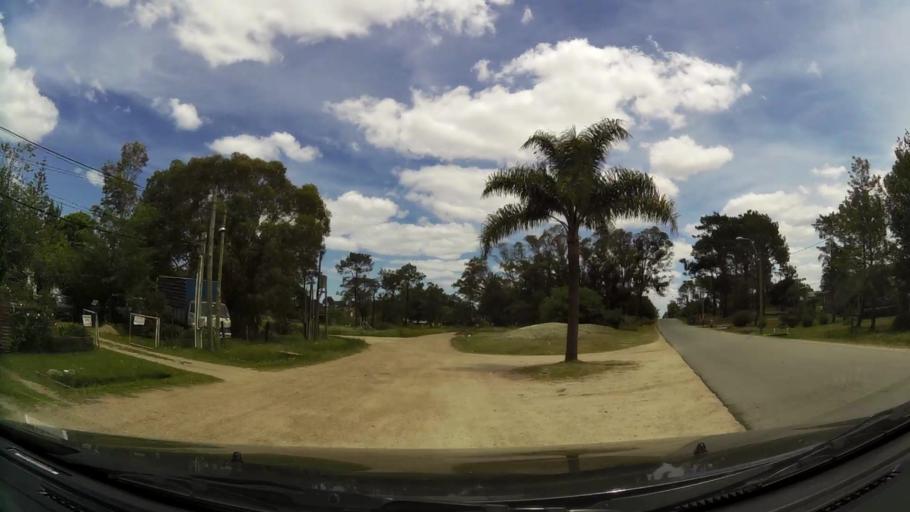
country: UY
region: Canelones
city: Empalme Olmos
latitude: -34.7986
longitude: -55.8902
